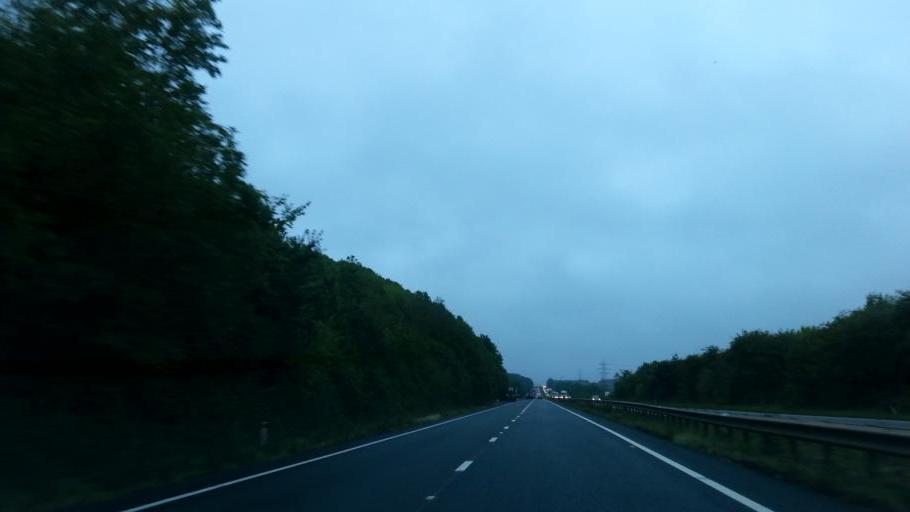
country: GB
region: England
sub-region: Lincolnshire
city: Great Gonerby
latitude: 52.9352
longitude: -0.6849
